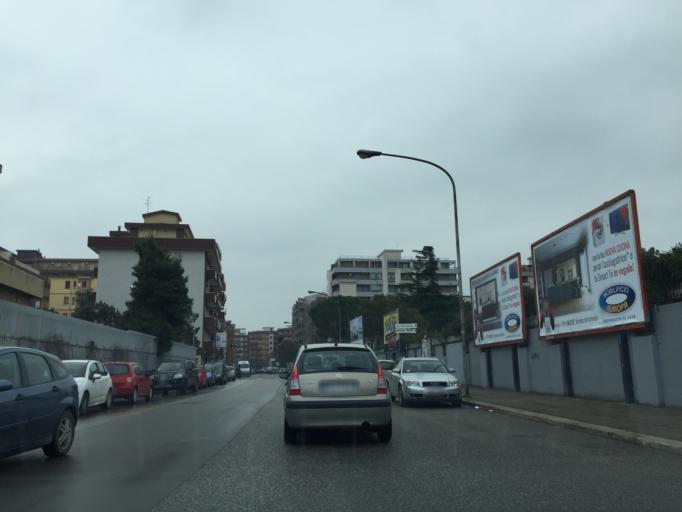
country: IT
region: Apulia
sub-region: Provincia di Foggia
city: Foggia
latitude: 41.4617
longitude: 15.5332
